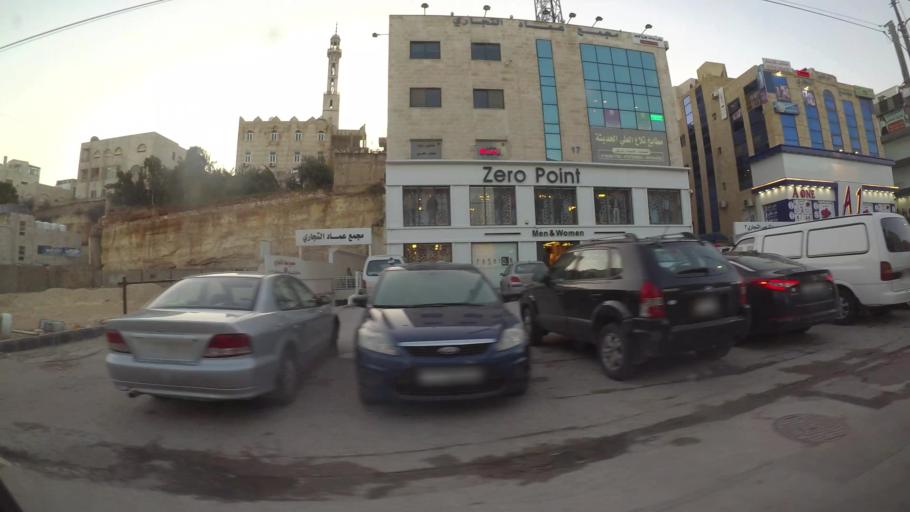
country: JO
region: Amman
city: Al Jubayhah
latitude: 31.9959
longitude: 35.8644
